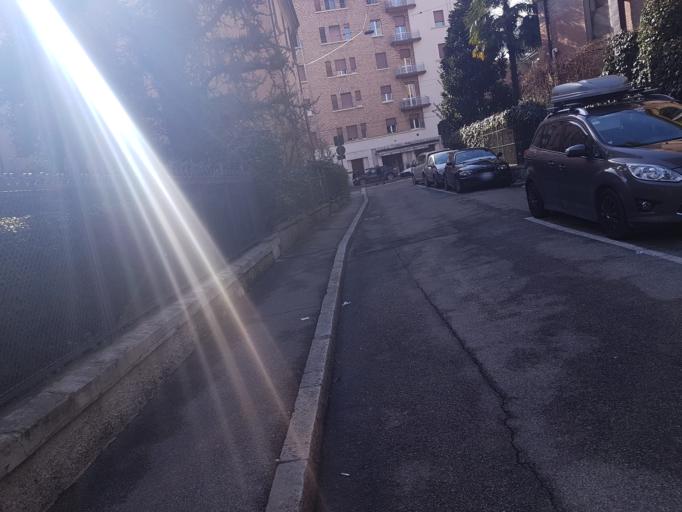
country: IT
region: Emilia-Romagna
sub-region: Provincia di Bologna
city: Bologna
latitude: 44.4960
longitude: 11.3216
